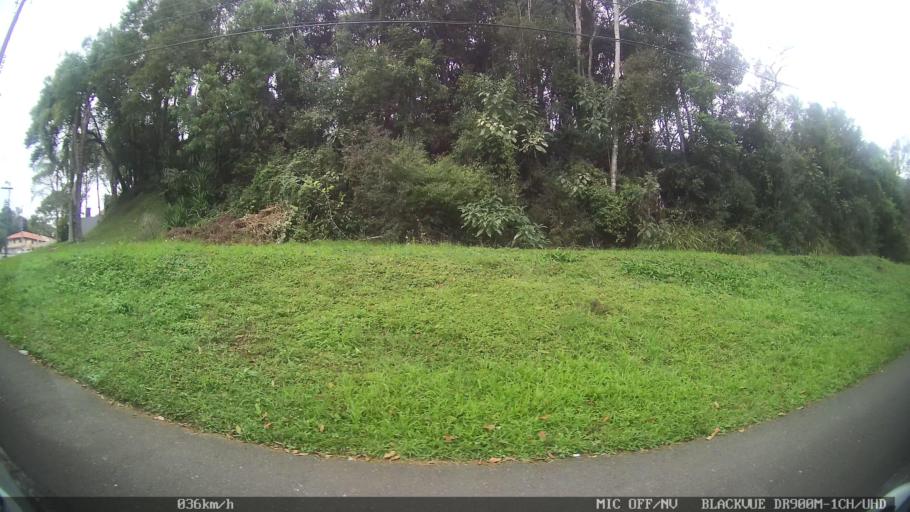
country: BR
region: Parana
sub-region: Almirante Tamandare
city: Almirante Tamandare
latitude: -25.3627
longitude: -49.2542
